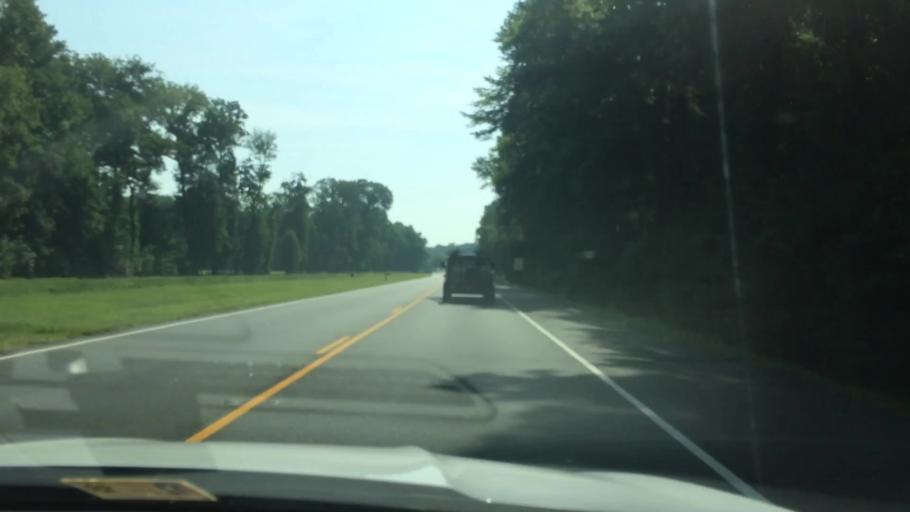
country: US
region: Virginia
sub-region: City of Poquoson
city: Poquoson
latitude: 37.1249
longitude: -76.3993
